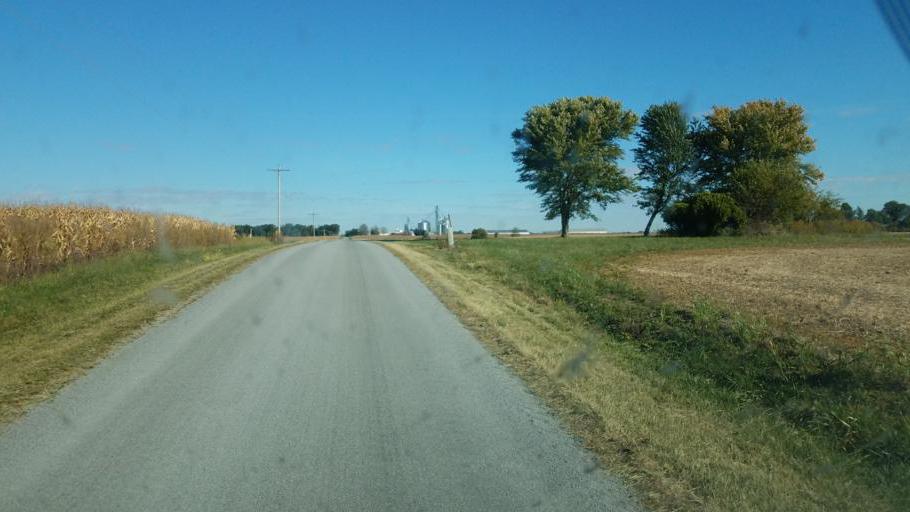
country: US
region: Ohio
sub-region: Marion County
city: Marion
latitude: 40.7053
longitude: -83.2073
